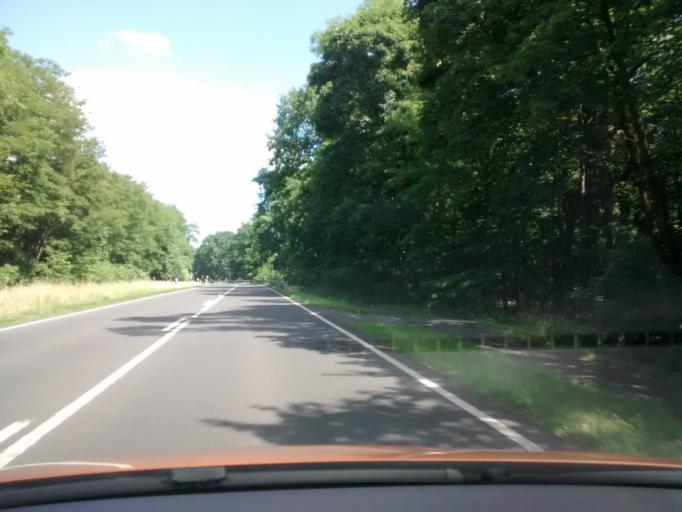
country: DE
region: Brandenburg
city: Potsdam
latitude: 52.4598
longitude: 13.0679
